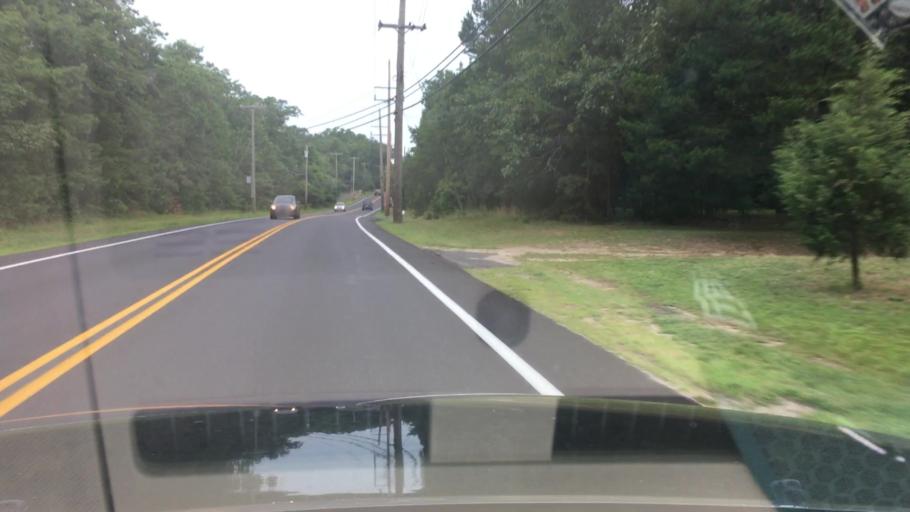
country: US
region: New Jersey
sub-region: Ocean County
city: Cedar Glen West
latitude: 40.0469
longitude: -74.3268
